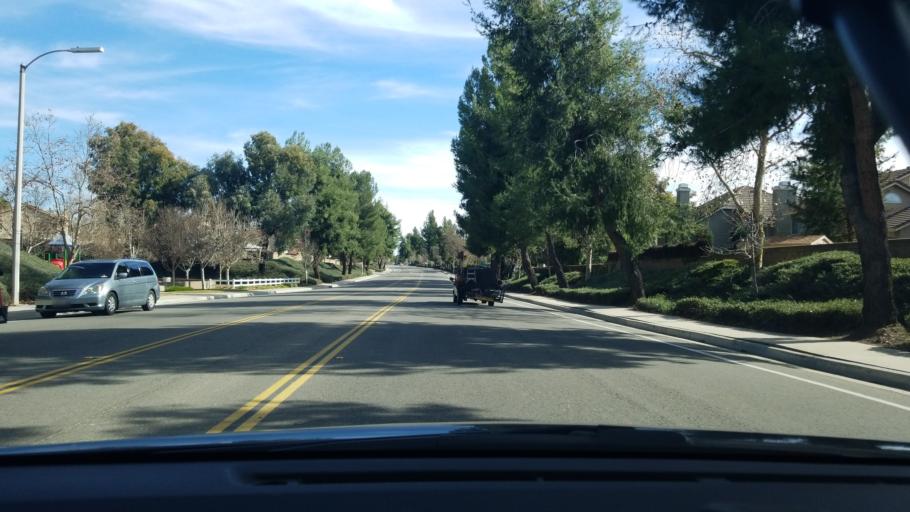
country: US
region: California
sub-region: Riverside County
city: Murrieta Hot Springs
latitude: 33.5748
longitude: -117.1748
